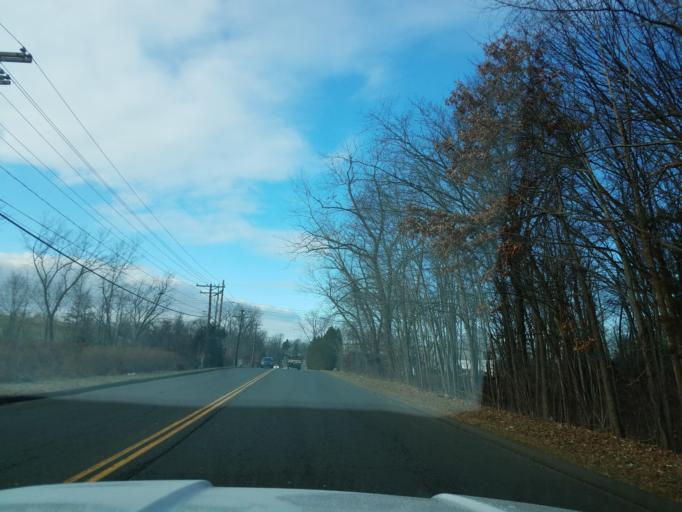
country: US
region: Connecticut
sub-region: Hartford County
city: Kensington
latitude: 41.6400
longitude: -72.7430
